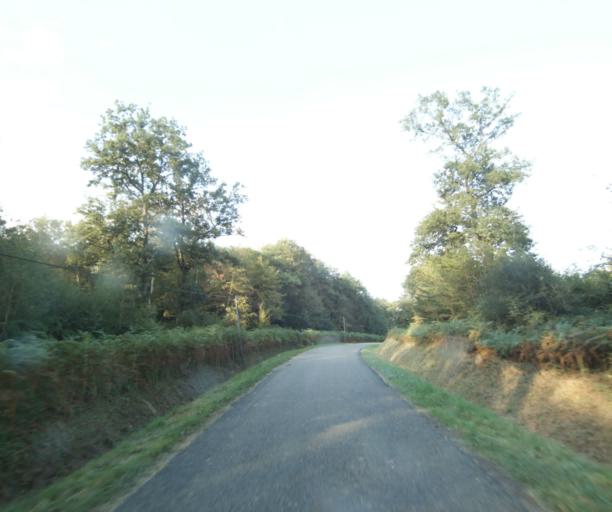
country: FR
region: Bourgogne
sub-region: Departement de Saone-et-Loire
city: Perrecy-les-Forges
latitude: 46.5914
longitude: 4.1816
